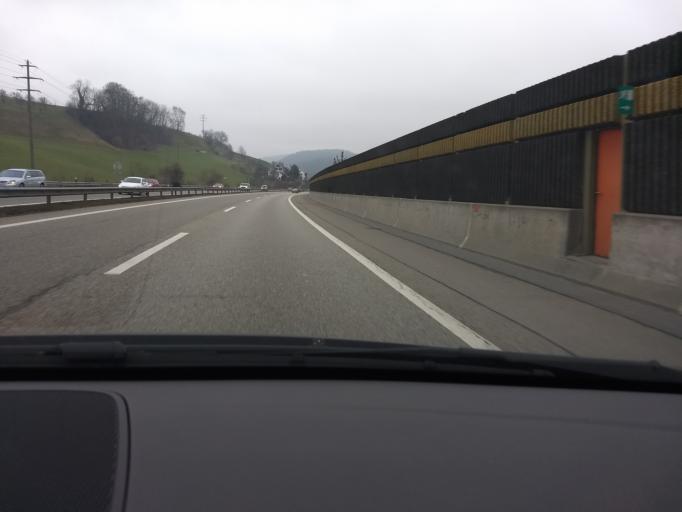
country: CH
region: Basel-Landschaft
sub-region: Bezirk Waldenburg
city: Diegten
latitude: 47.4074
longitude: 7.8070
